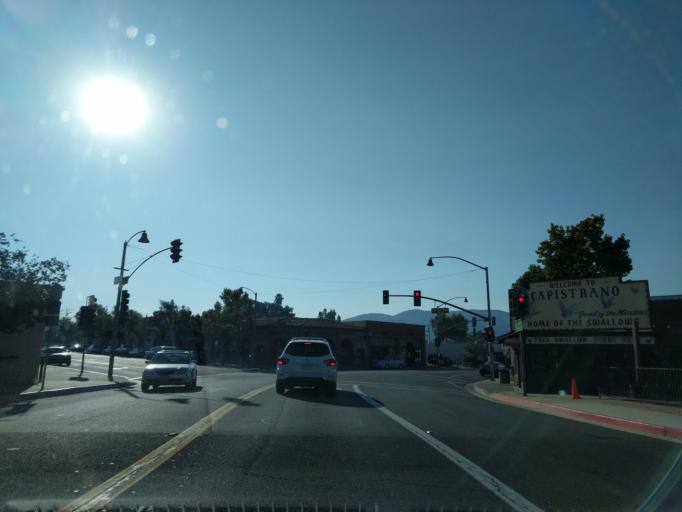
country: US
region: California
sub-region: Orange County
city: San Juan Capistrano
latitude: 33.5021
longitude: -117.6631
